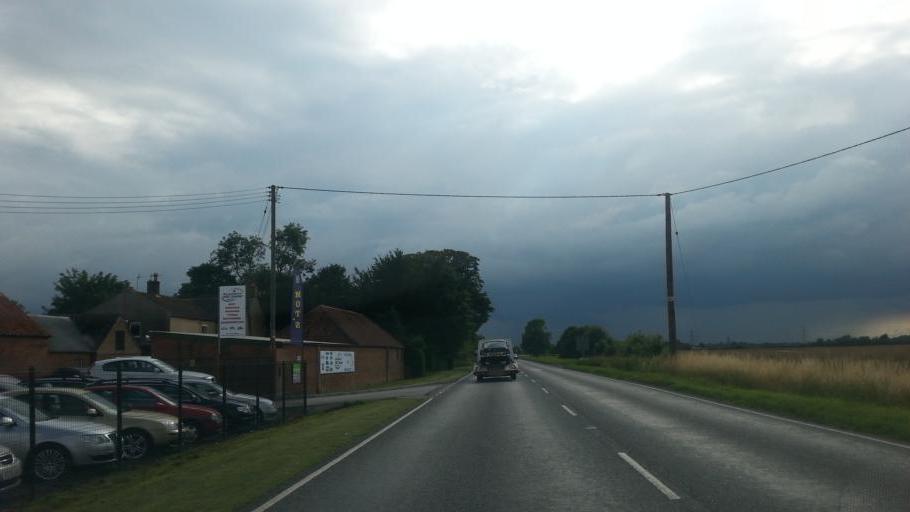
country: GB
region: England
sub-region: Lincolnshire
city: Heckington
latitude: 52.9822
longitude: -0.2522
